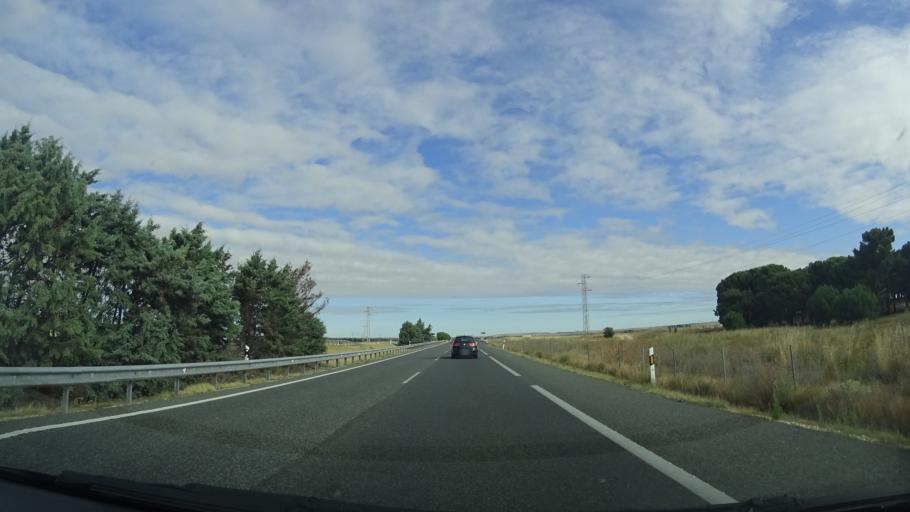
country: ES
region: Castille and Leon
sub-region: Provincia de Valladolid
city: San Vicente del Palacio
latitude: 41.2630
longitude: -4.8794
